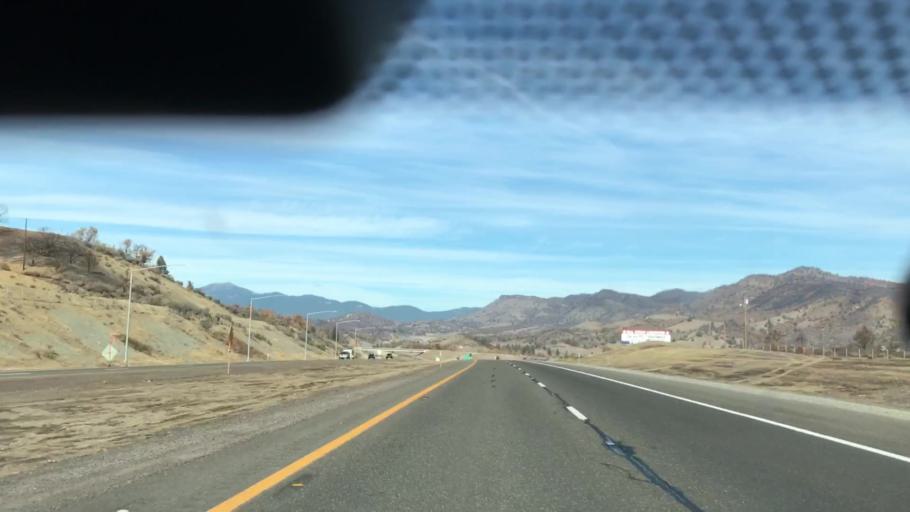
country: US
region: California
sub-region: Siskiyou County
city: Yreka
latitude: 41.9114
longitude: -122.5698
